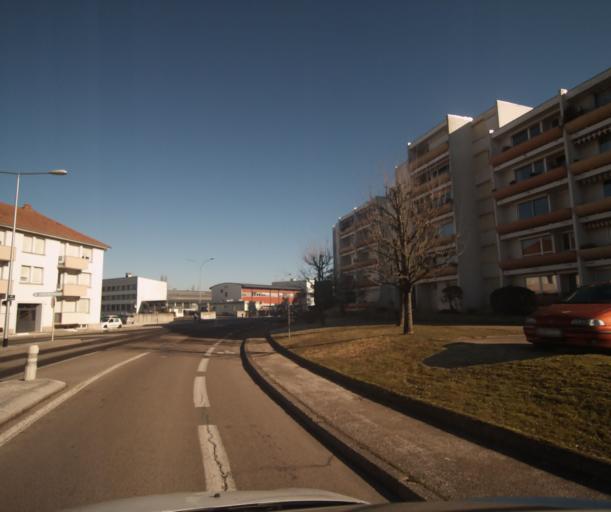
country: FR
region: Franche-Comte
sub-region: Departement du Doubs
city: Besancon
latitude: 47.2348
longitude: 5.9938
